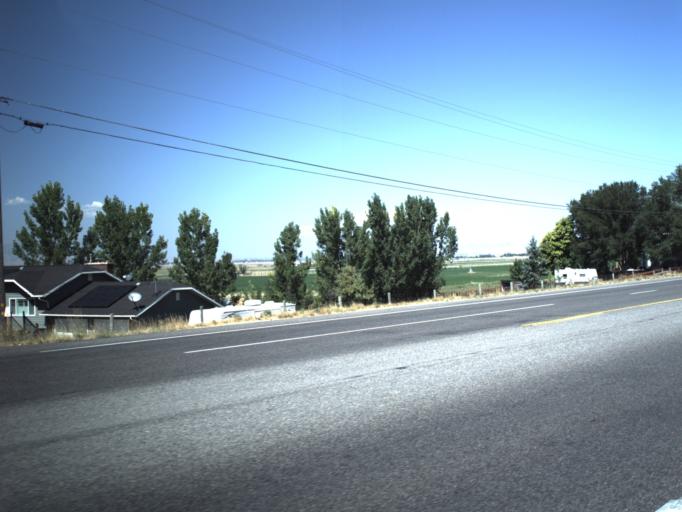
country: US
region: Utah
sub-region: Cache County
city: Smithfield
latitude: 41.8793
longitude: -111.8219
